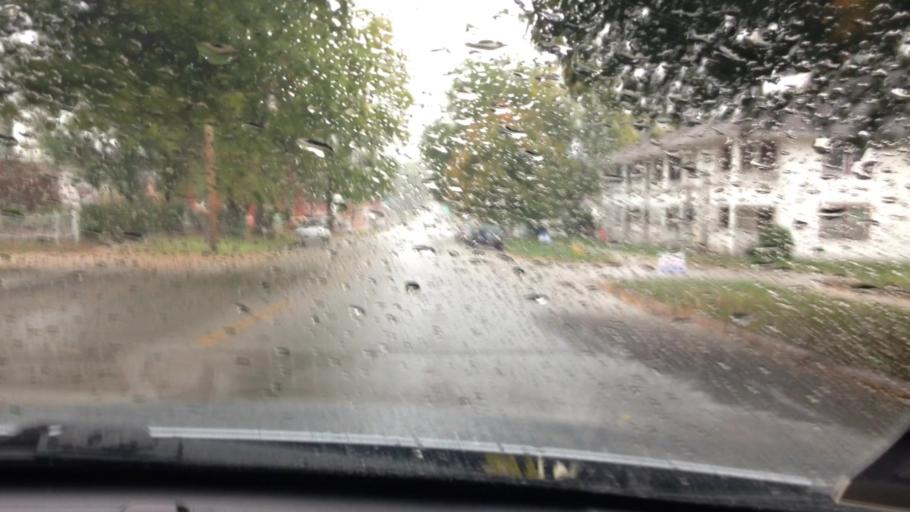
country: US
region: Kansas
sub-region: Leavenworth County
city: Leavenworth
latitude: 39.3201
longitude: -94.9218
